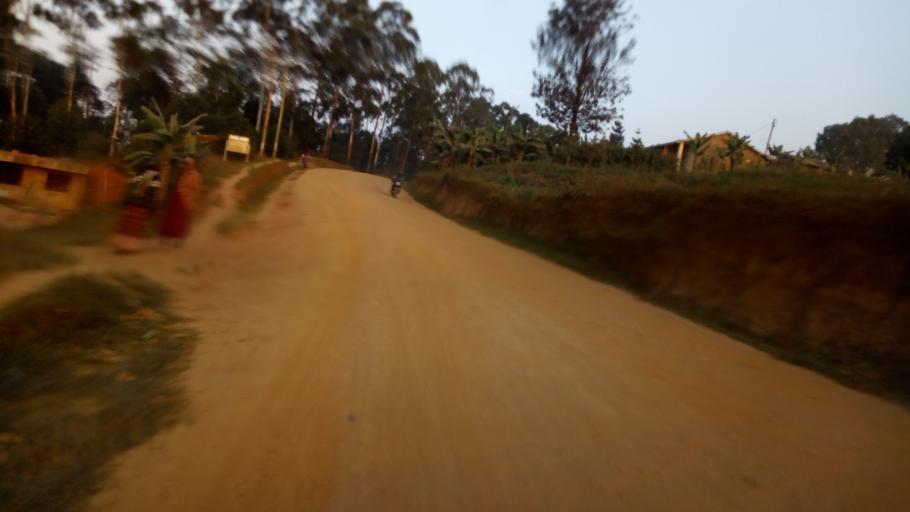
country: UG
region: Western Region
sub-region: Rukungiri District
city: Rukungiri
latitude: -0.7794
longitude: 29.9244
